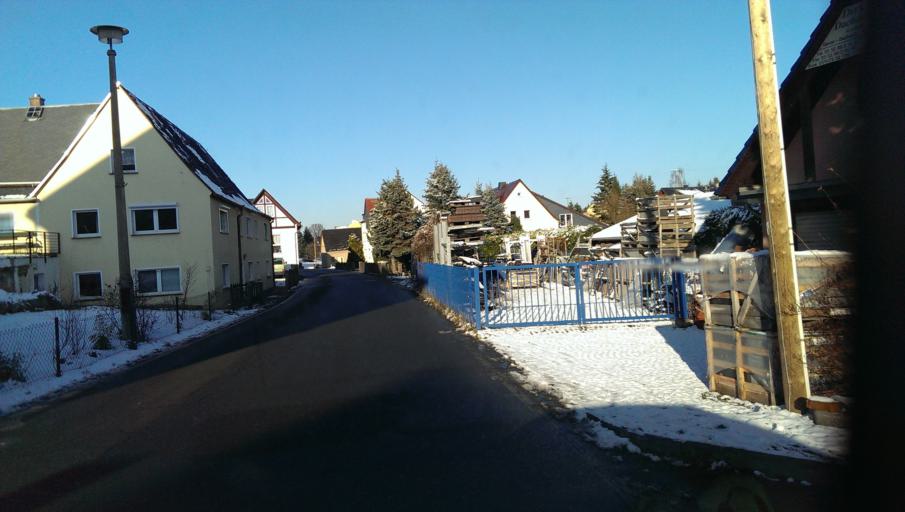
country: DE
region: Saxony
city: Dorfhain
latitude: 50.9207
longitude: 13.5895
